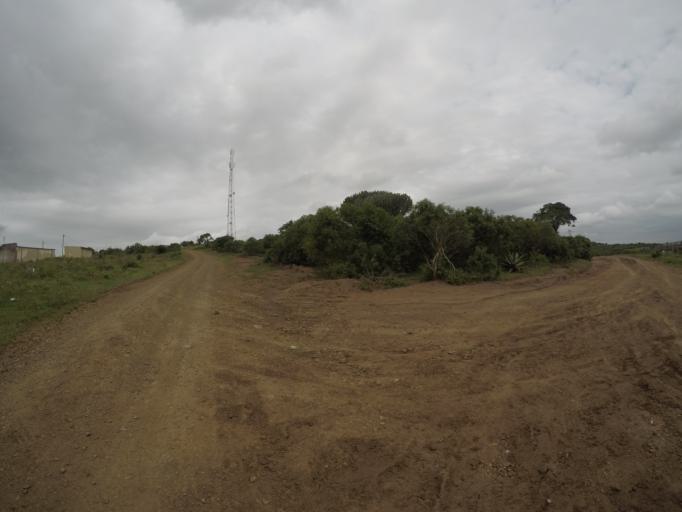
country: ZA
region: KwaZulu-Natal
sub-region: uThungulu District Municipality
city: Empangeni
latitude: -28.6030
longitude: 31.8347
